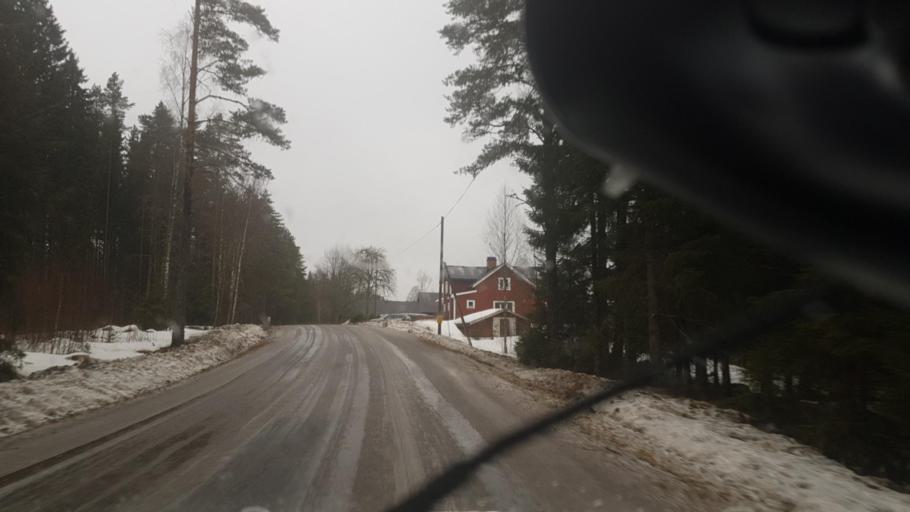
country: SE
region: Vaermland
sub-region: Eda Kommun
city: Charlottenberg
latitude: 59.8822
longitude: 12.3550
